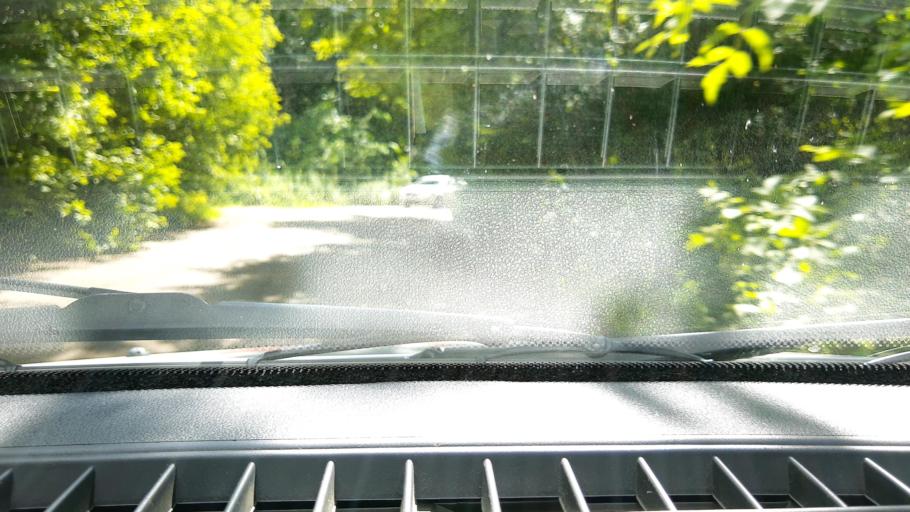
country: RU
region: Bashkortostan
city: Ufa
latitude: 54.6912
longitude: 56.0526
